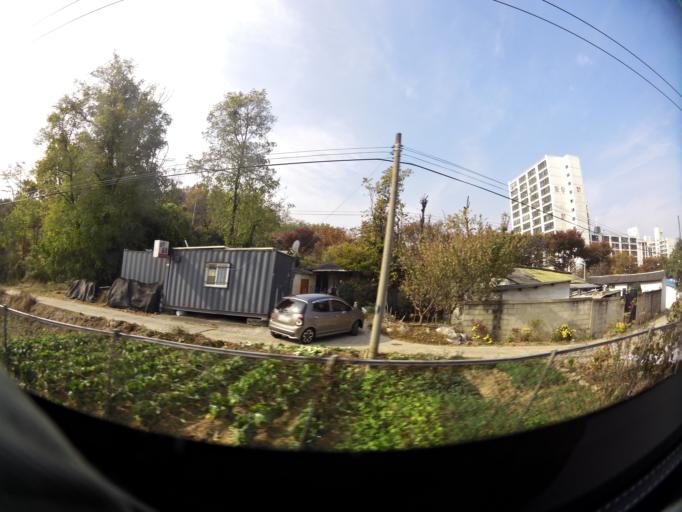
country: KR
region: Gyeongsangbuk-do
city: Gumi
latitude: 36.1078
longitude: 128.3579
